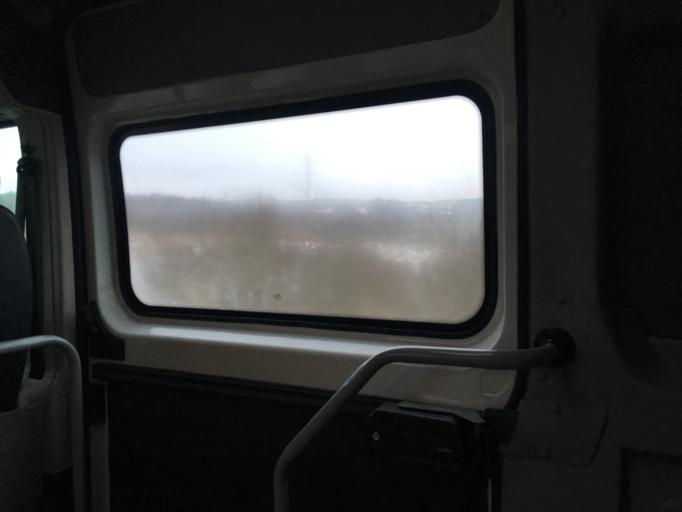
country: RU
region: Tula
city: Krapivna
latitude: 54.1124
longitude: 37.2091
